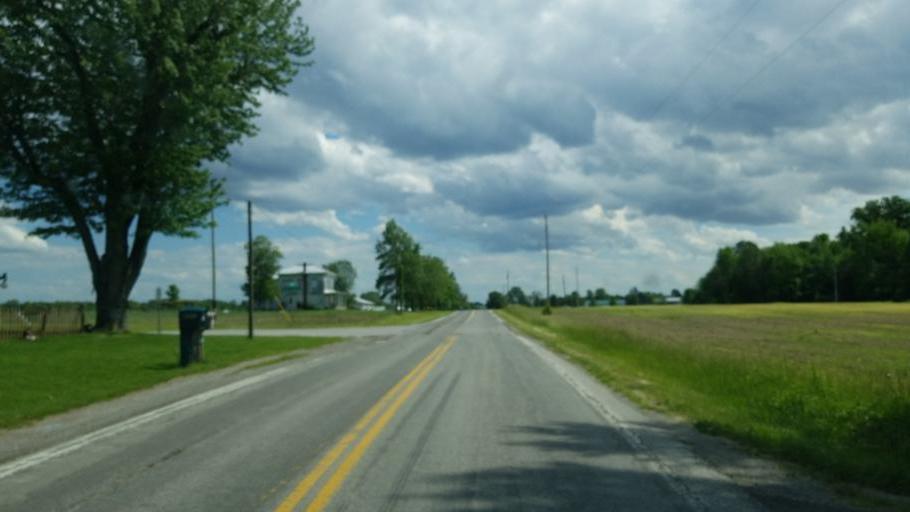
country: US
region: Ohio
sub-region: Huron County
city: Plymouth
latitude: 41.0082
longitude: -82.6067
